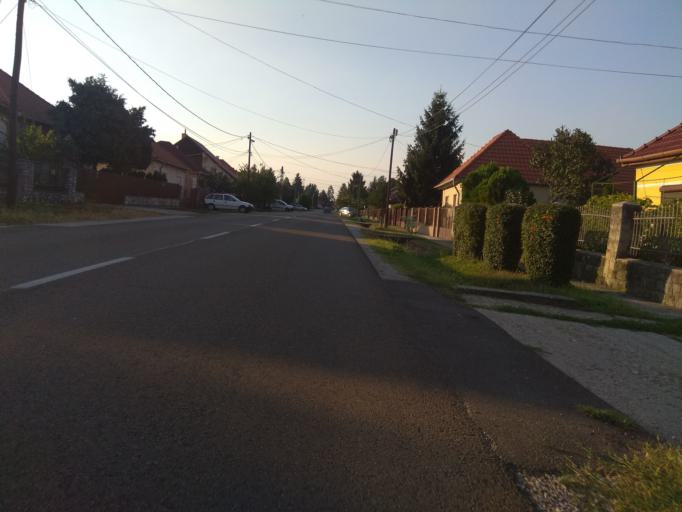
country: HU
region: Borsod-Abauj-Zemplen
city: Nyekladhaza
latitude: 47.9883
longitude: 20.8384
